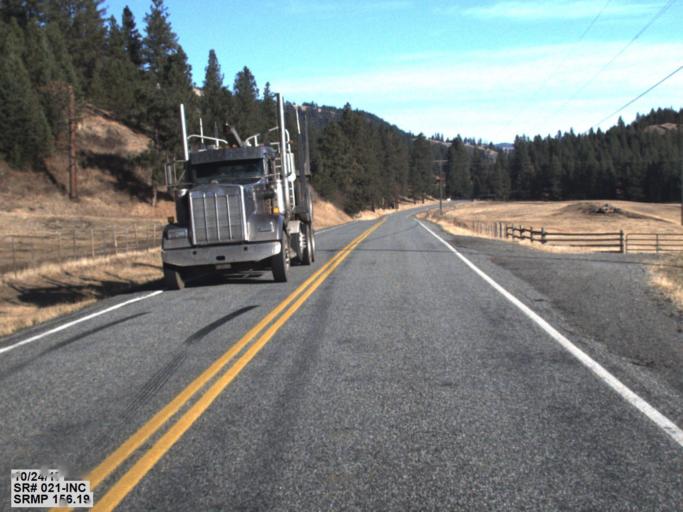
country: US
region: Washington
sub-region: Ferry County
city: Republic
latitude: 48.5867
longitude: -118.7424
